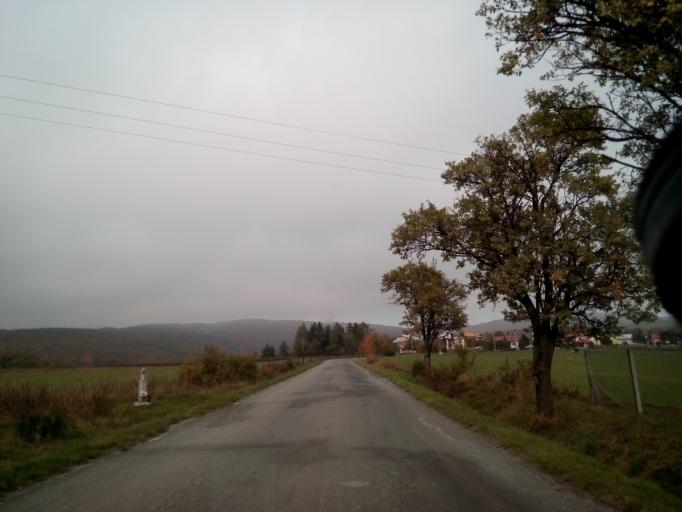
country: SK
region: Kosicky
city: Kosice
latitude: 48.7386
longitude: 21.1227
